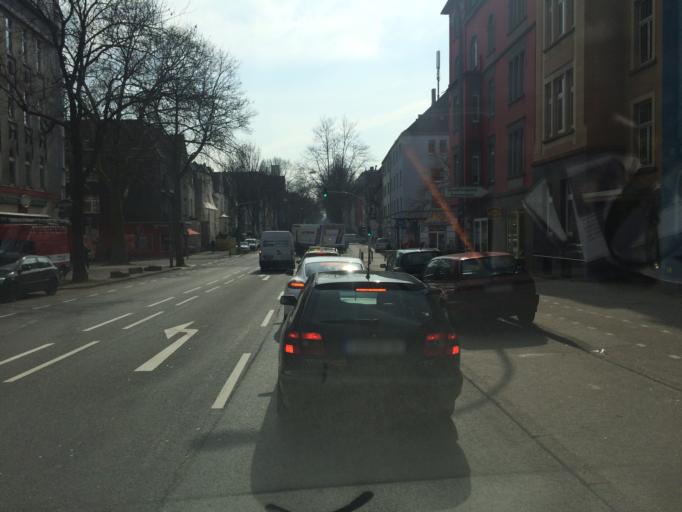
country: DE
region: North Rhine-Westphalia
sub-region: Regierungsbezirk Arnsberg
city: Dortmund
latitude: 51.5059
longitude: 7.4511
